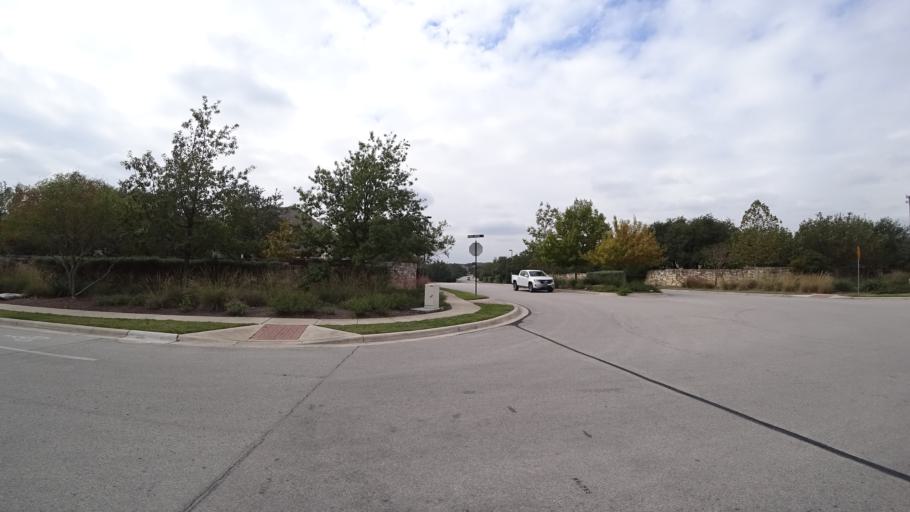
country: US
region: Texas
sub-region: Travis County
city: Shady Hollow
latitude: 30.1993
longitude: -97.9167
